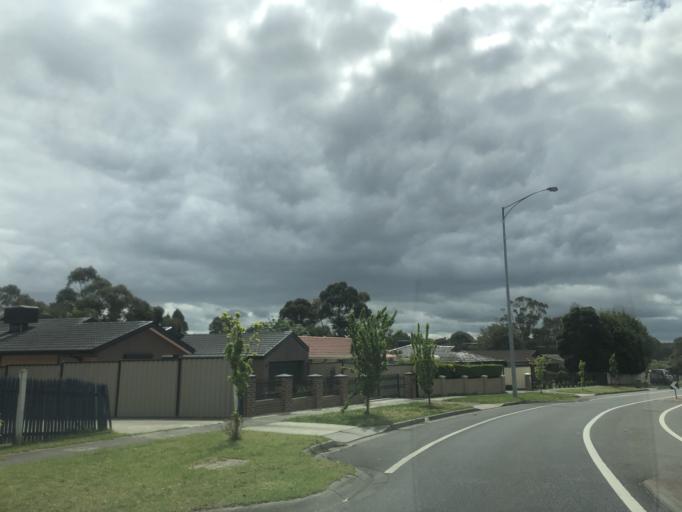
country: AU
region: Victoria
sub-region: Casey
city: Endeavour Hills
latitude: -37.9809
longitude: 145.2453
